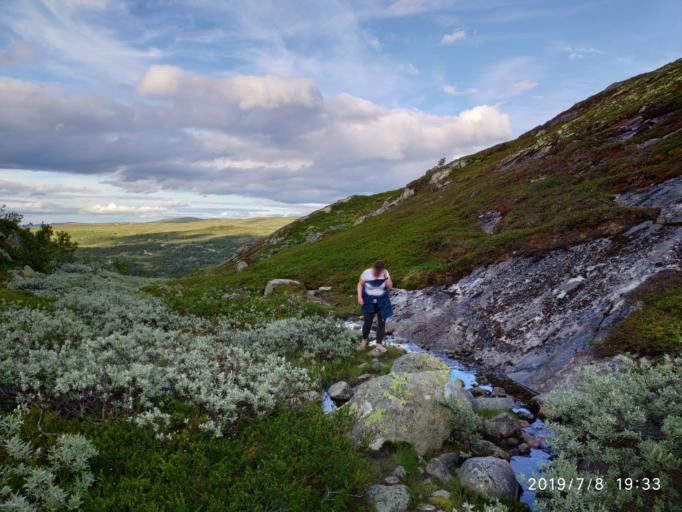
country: NO
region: Buskerud
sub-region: Nes
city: Nesbyen
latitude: 60.3471
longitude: 9.1676
